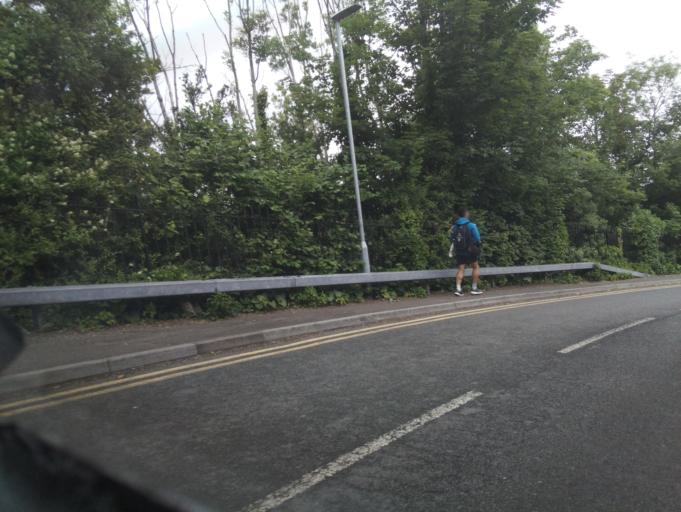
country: GB
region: Wales
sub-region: Vale of Glamorgan
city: Penarth
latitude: 51.4447
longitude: -3.1703
